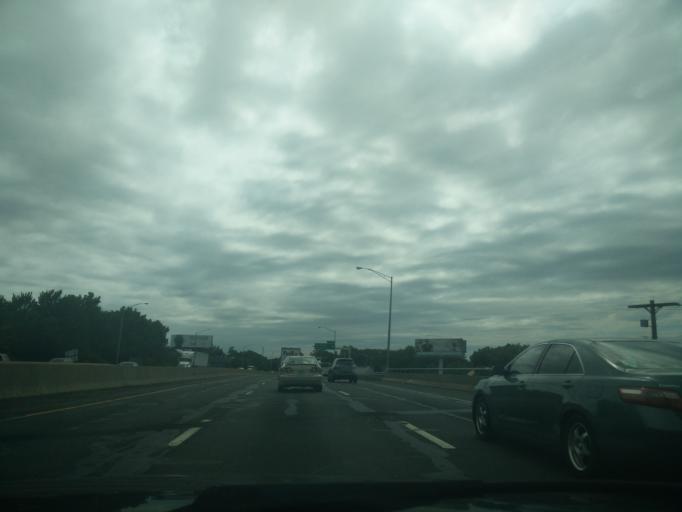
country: US
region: Connecticut
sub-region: Fairfield County
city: Stratford
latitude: 41.1871
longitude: -73.1367
